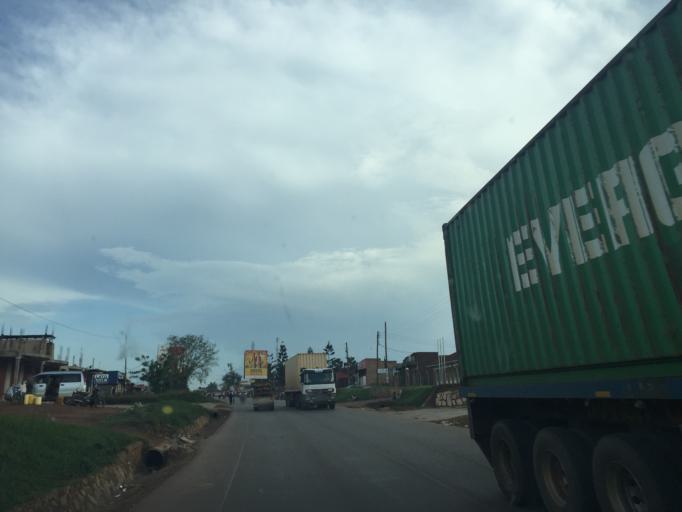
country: UG
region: Central Region
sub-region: Luwero District
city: Luwero
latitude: 0.8505
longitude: 32.4875
